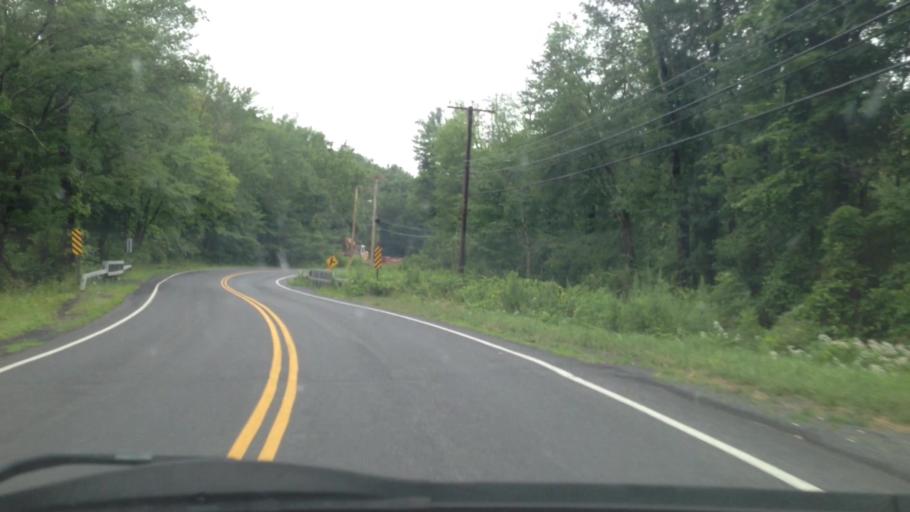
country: US
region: New York
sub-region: Ulster County
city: Highland
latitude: 41.7376
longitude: -74.0105
